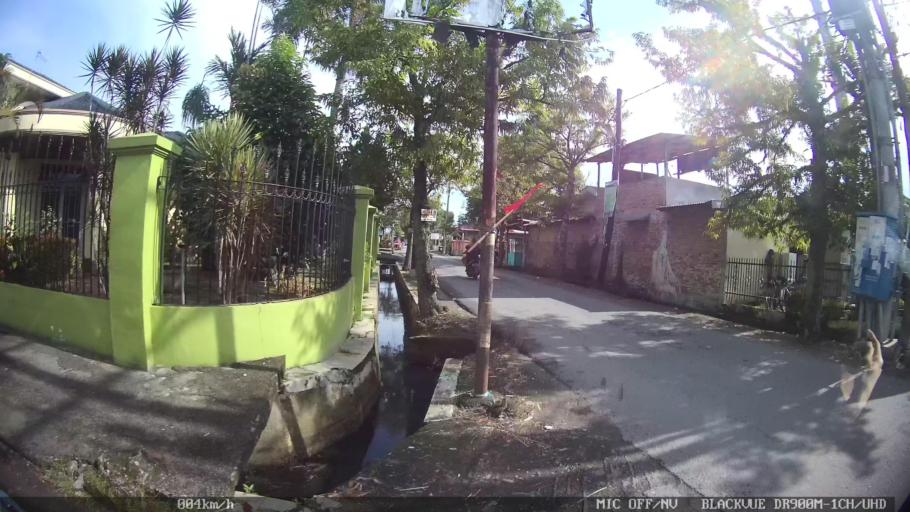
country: ID
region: North Sumatra
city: Medan
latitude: 3.6115
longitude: 98.6573
